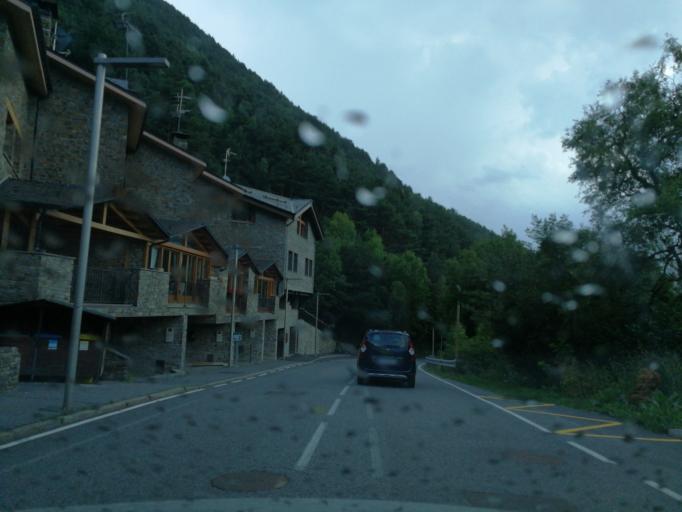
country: AD
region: Ordino
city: Ordino
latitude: 42.5527
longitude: 1.5402
